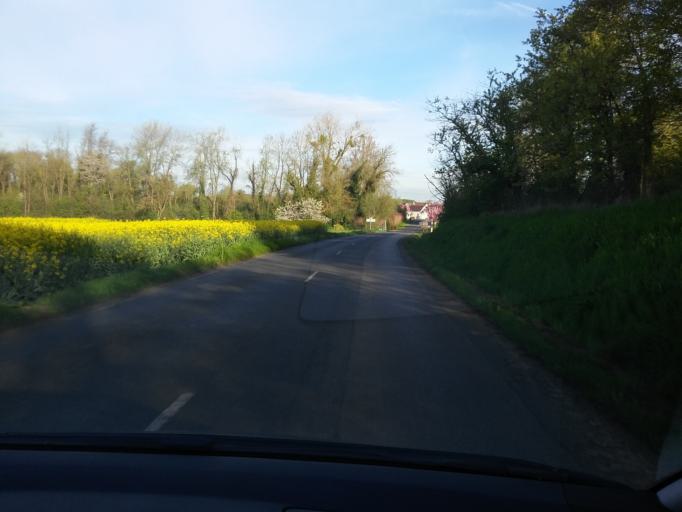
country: FR
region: Picardie
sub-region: Departement de l'Oise
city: Longueil-Sainte-Marie
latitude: 49.3490
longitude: 2.7244
